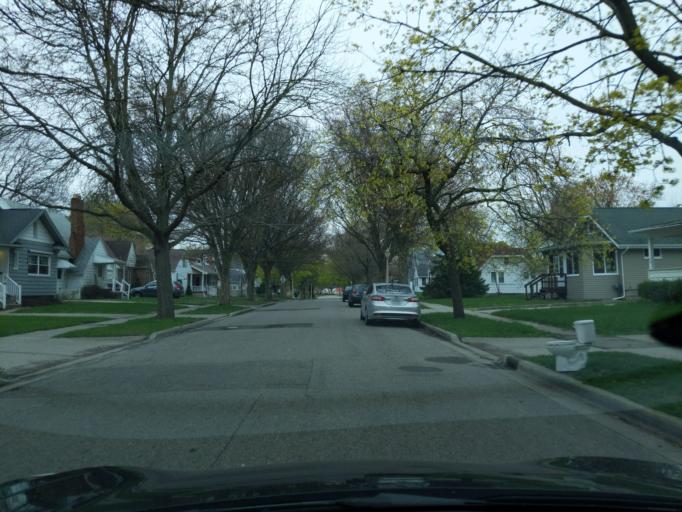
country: US
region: Michigan
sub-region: Ingham County
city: Edgemont Park
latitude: 42.7447
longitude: -84.5766
